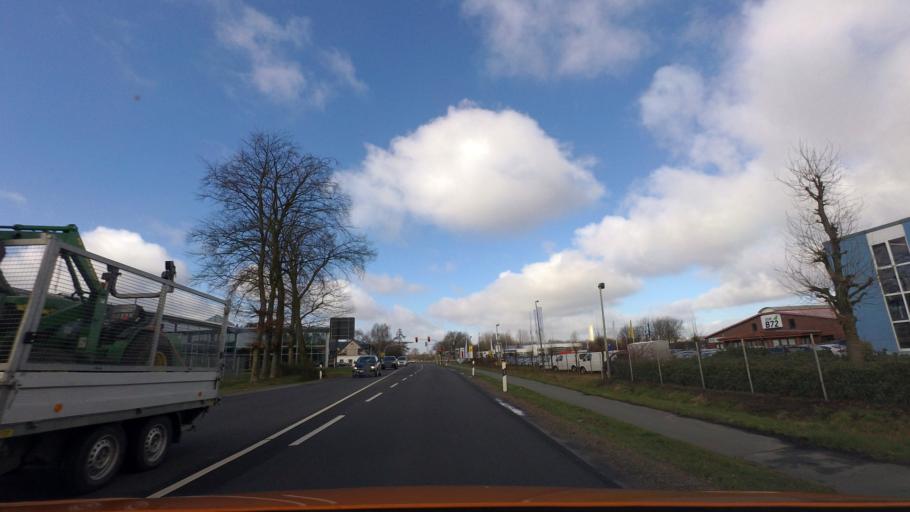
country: DE
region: Lower Saxony
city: Cappeln
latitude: 52.8294
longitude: 8.1169
